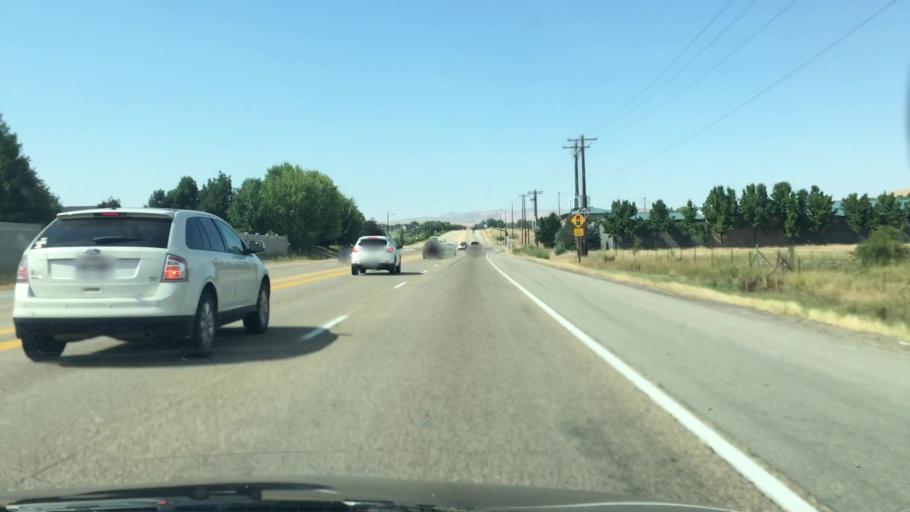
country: US
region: Idaho
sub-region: Ada County
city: Eagle
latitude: 43.6909
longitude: -116.3192
